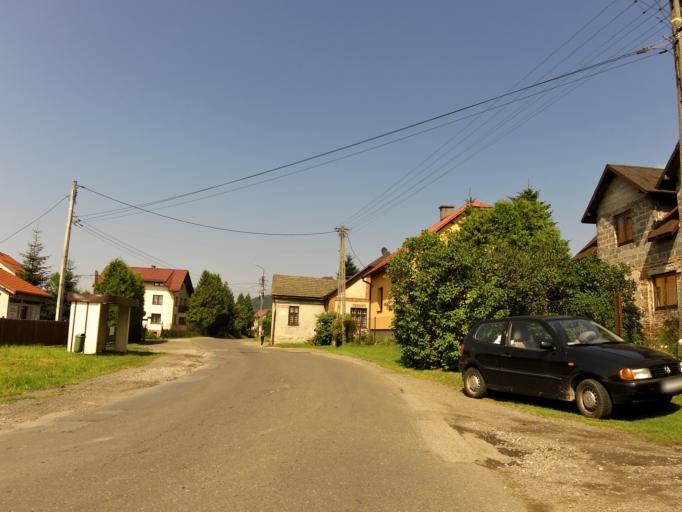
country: PL
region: Silesian Voivodeship
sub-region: Powiat zywiecki
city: Wieprz
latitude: 49.6389
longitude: 19.1758
